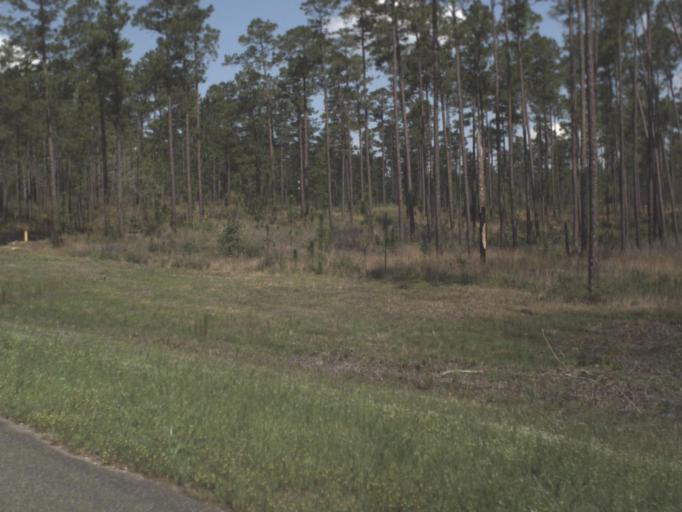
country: US
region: Florida
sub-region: Santa Rosa County
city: Point Baker
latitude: 30.8794
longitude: -86.9516
